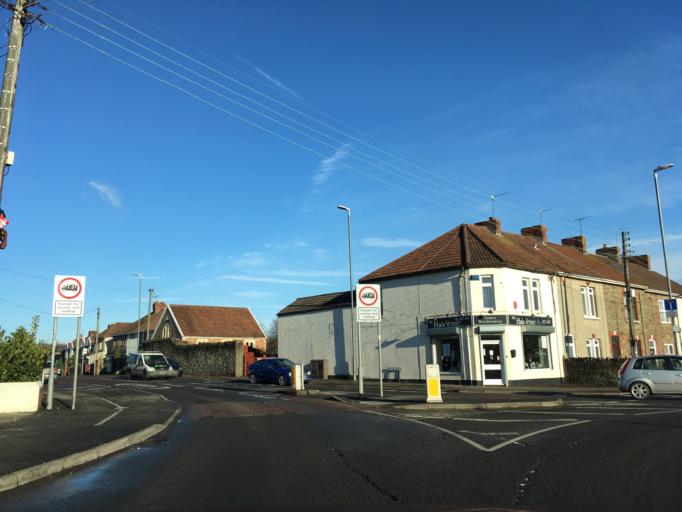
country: GB
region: England
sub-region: South Gloucestershire
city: Kingswood
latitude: 51.4676
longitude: -2.4895
